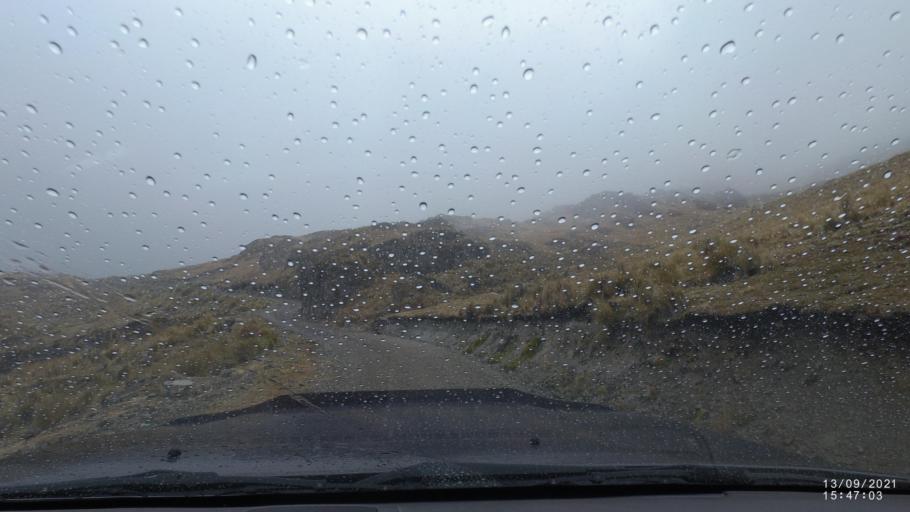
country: BO
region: Cochabamba
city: Colomi
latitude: -17.3142
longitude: -65.7194
